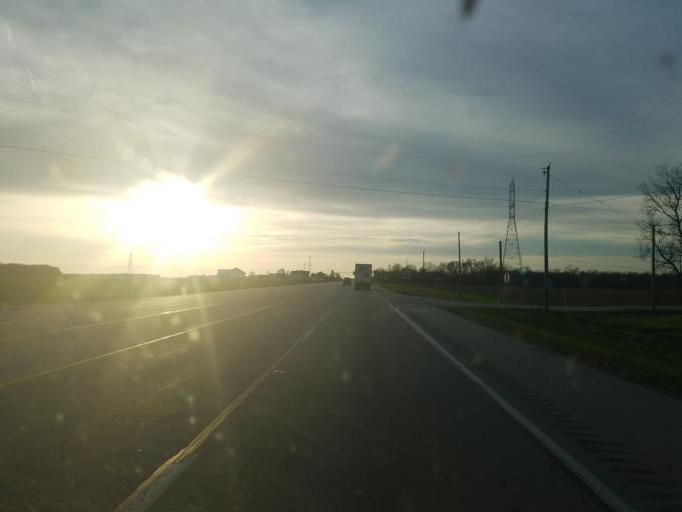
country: US
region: Ohio
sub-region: Wood County
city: Luckey
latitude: 41.4796
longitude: -83.4338
